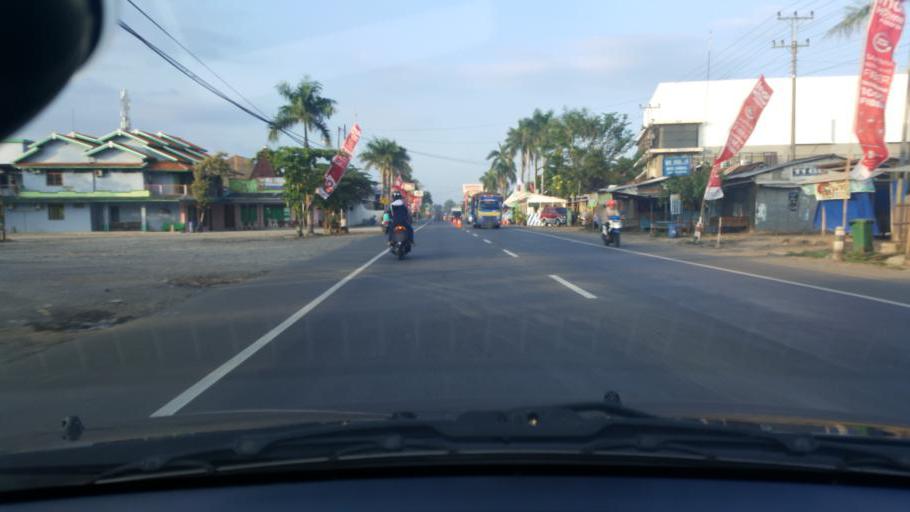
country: ID
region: Central Java
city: Gemiring
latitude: -6.7823
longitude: 110.9876
